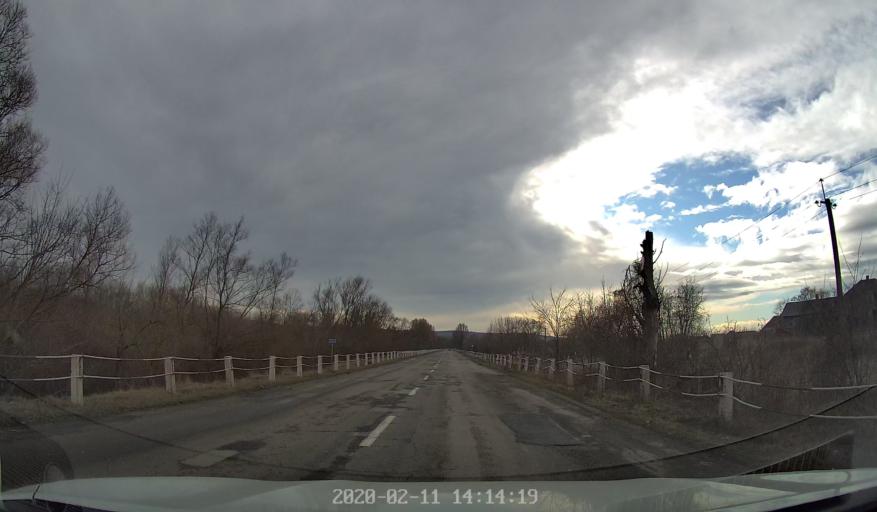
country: RO
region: Botosani
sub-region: Comuna Hudesti
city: Alba
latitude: 48.2197
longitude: 26.4617
